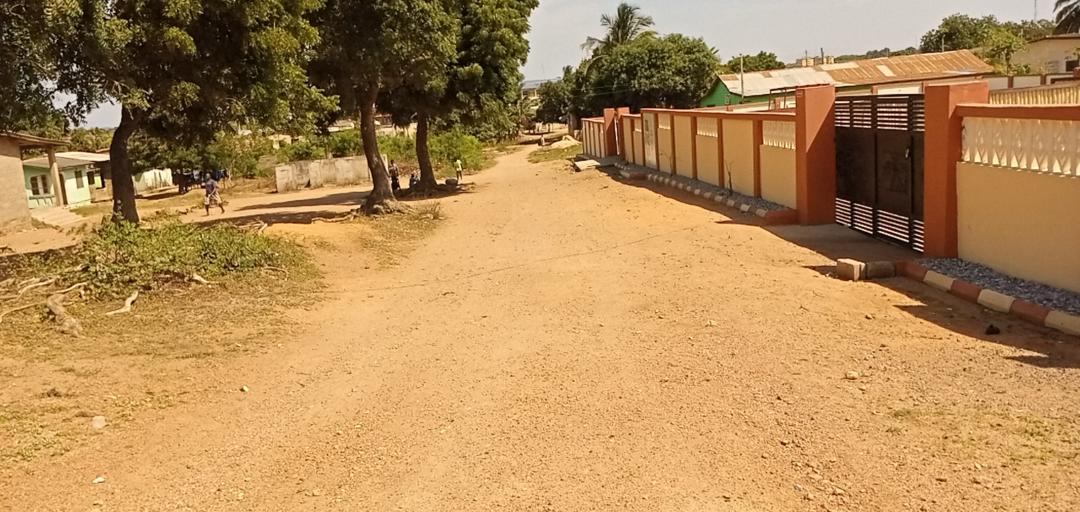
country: GH
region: Central
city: Winneba
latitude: 5.3535
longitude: -0.6190
